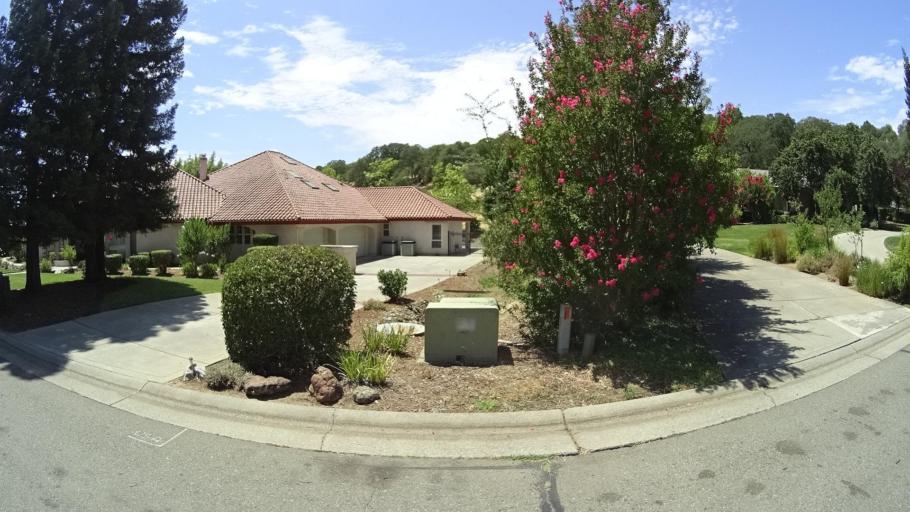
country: US
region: California
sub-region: Placer County
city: Rocklin
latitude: 38.8219
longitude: -121.2323
